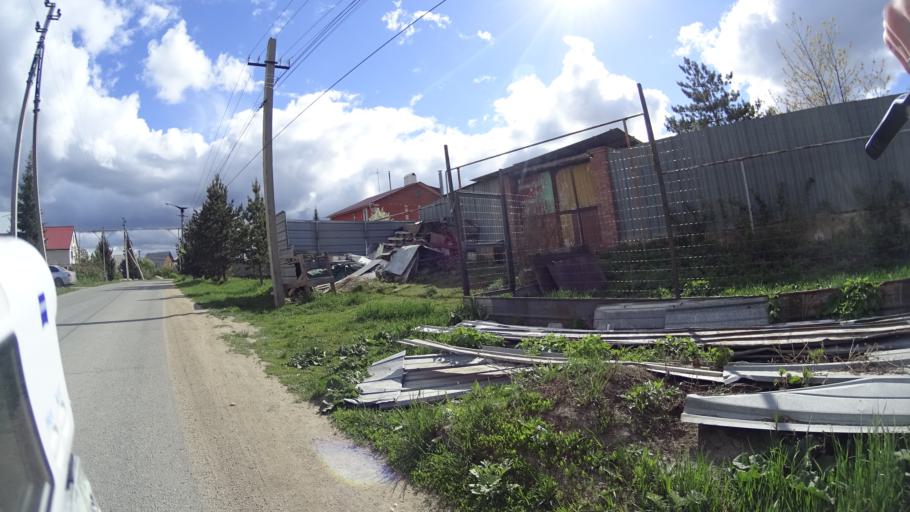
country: RU
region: Chelyabinsk
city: Sargazy
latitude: 55.1487
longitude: 61.2375
